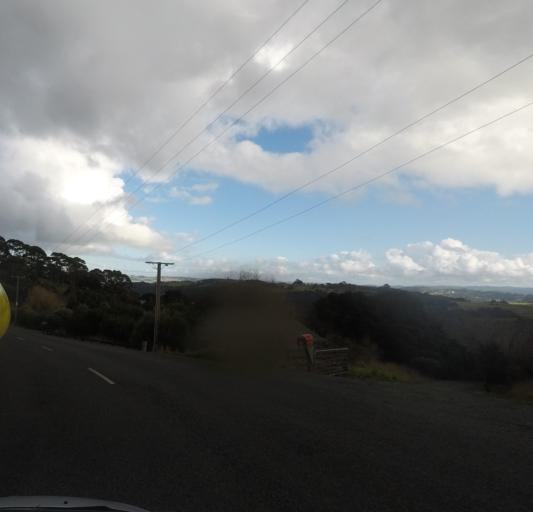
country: NZ
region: Auckland
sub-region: Auckland
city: Warkworth
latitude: -36.3759
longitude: 174.7599
